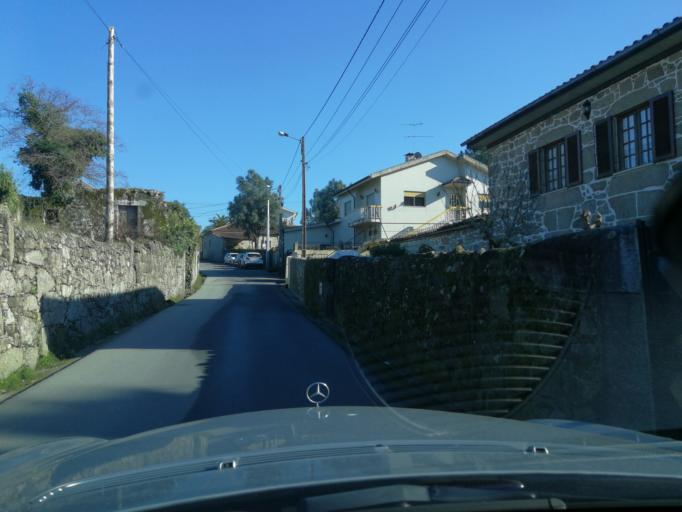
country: PT
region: Braga
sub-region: Braga
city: Adaufe
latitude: 41.6151
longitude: -8.4081
